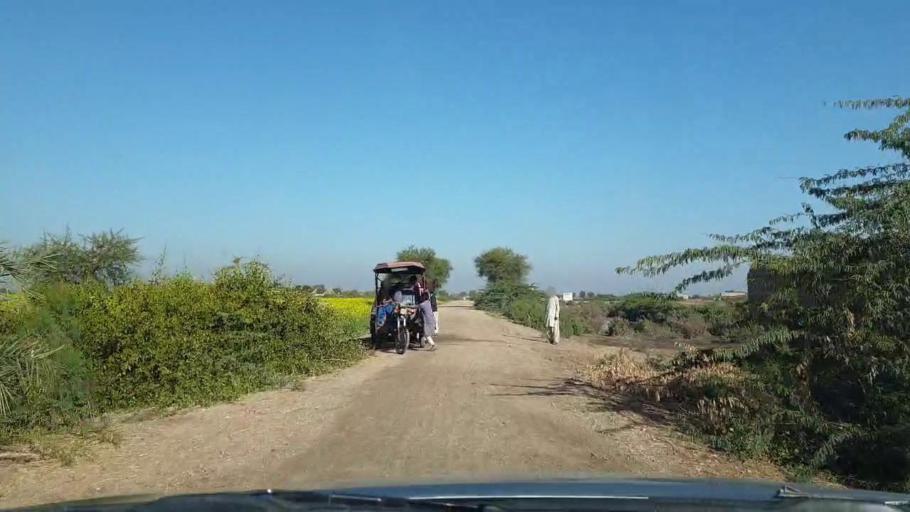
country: PK
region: Sindh
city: Jhol
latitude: 25.8163
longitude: 68.9652
